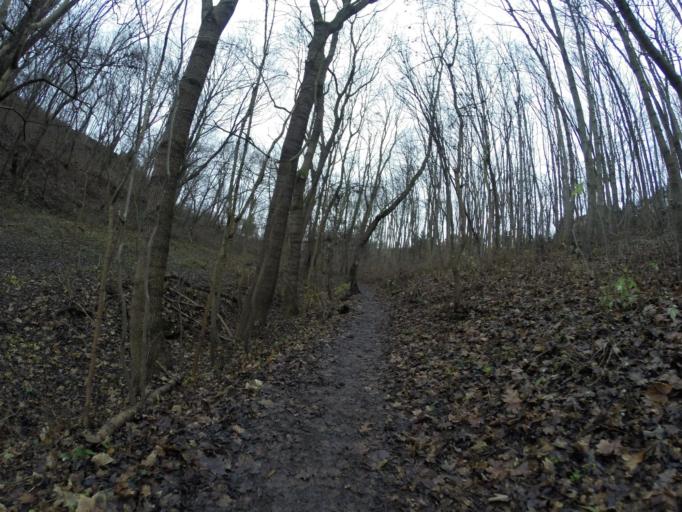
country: DE
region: Thuringia
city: Jena
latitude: 50.9274
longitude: 11.6032
